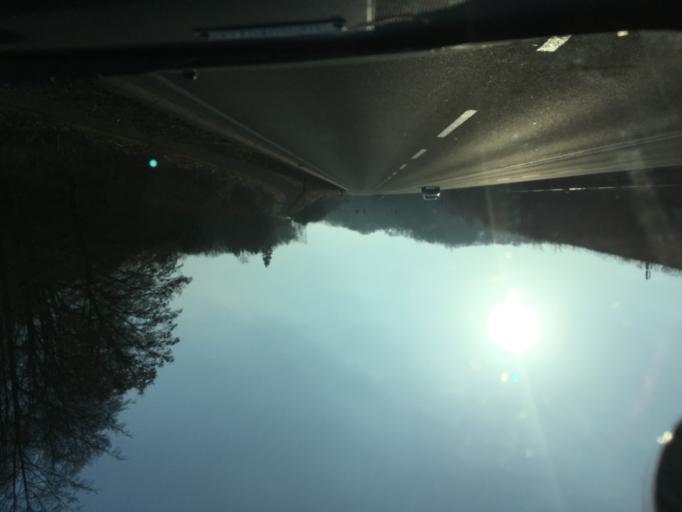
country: DE
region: North Rhine-Westphalia
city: Schwerte
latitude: 51.4715
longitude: 7.5504
